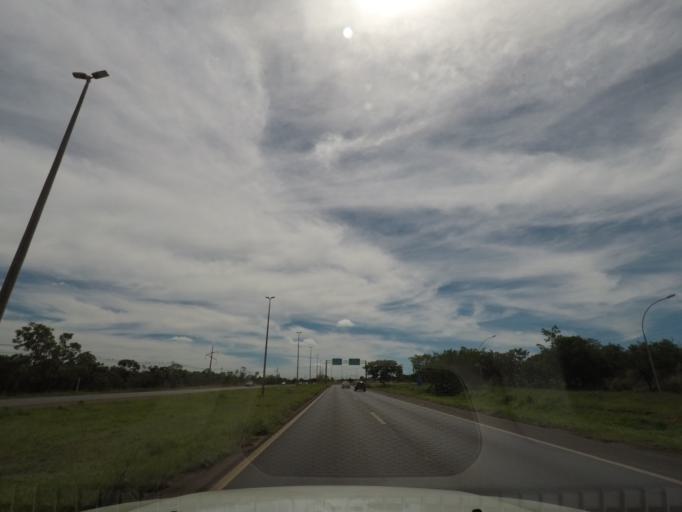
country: BR
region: Goias
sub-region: Planaltina
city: Planaltina
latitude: -15.5947
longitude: -47.6591
